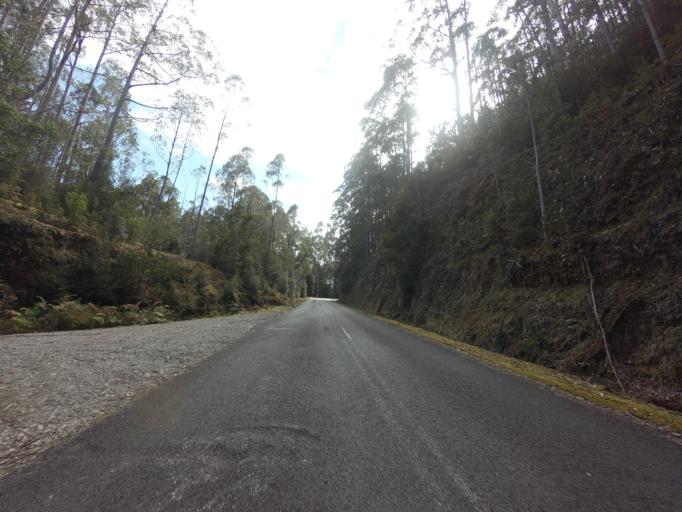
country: AU
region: Tasmania
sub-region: Huon Valley
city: Geeveston
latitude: -42.8176
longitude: 146.3453
